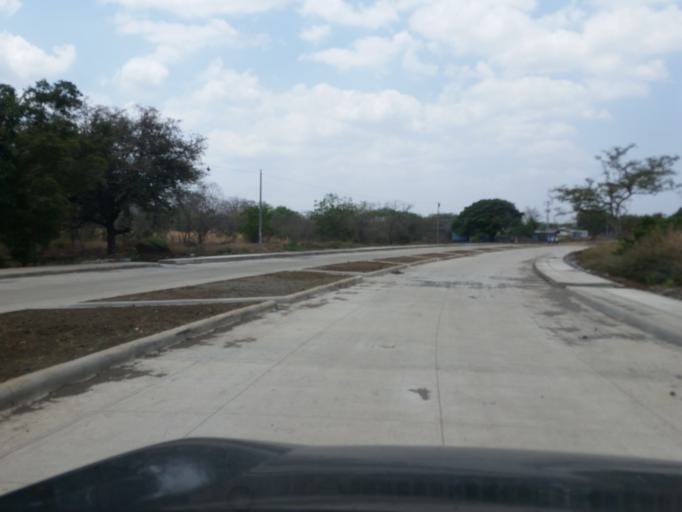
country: NI
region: Managua
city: Managua
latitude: 12.1325
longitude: -86.1853
